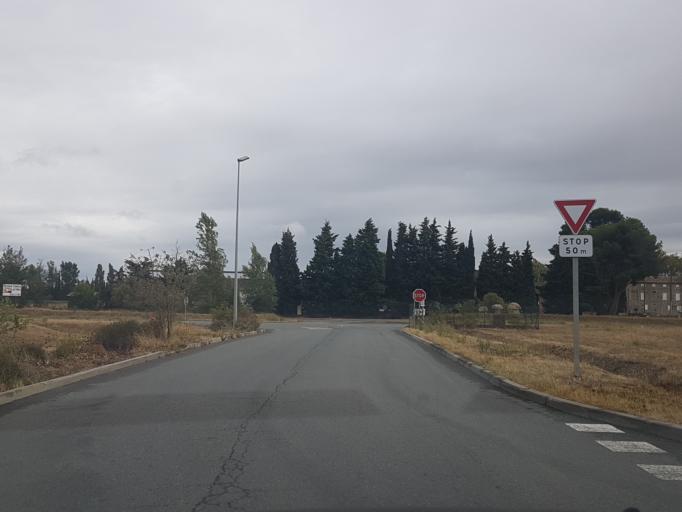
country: FR
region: Languedoc-Roussillon
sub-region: Departement de l'Aude
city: Bram
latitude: 43.2413
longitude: 2.0976
